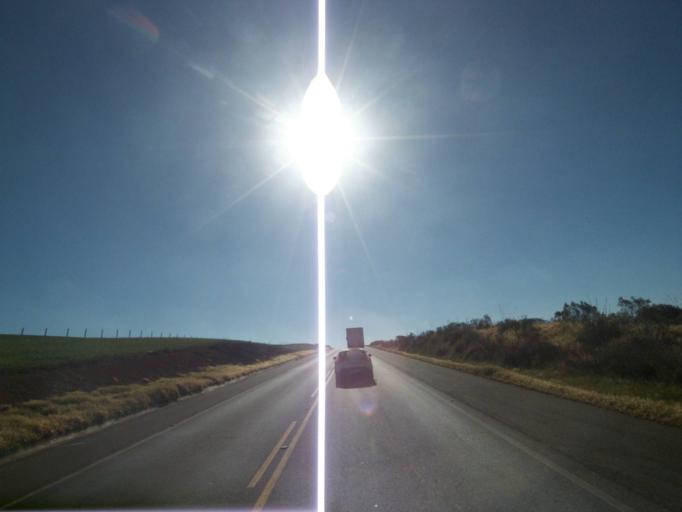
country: BR
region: Parana
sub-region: Tibagi
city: Tibagi
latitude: -24.6416
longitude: -50.4569
